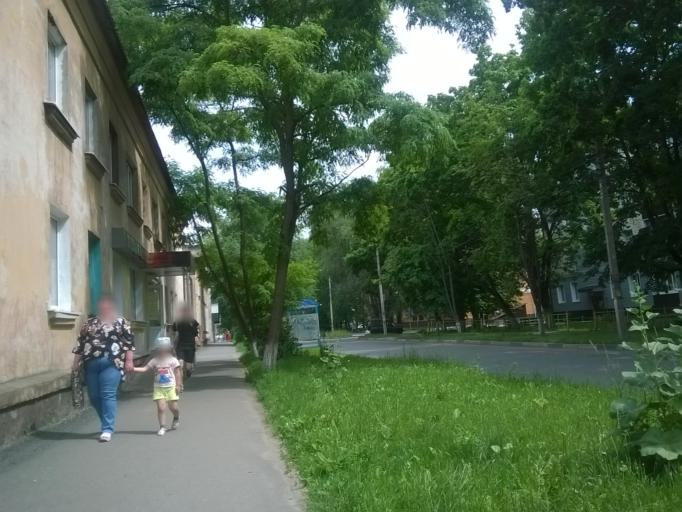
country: RU
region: Kursk
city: Kursk
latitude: 51.6744
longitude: 36.1520
